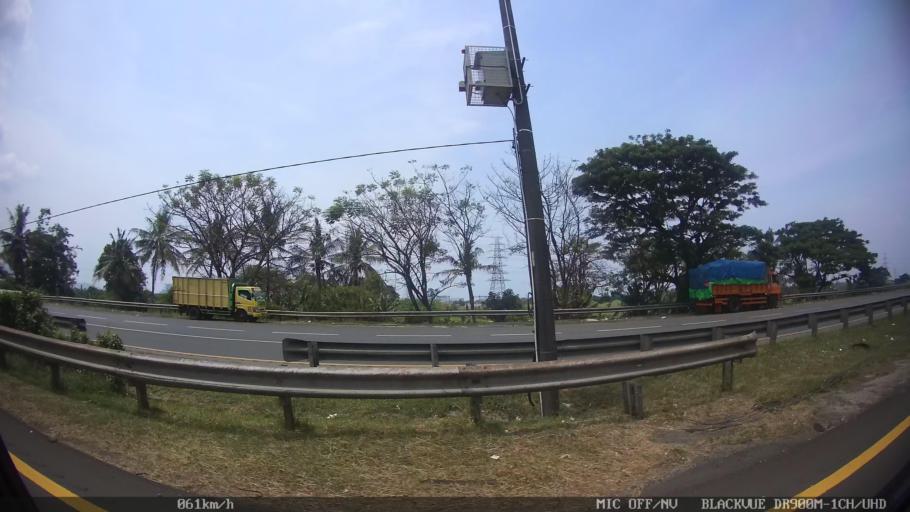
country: ID
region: Banten
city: Bojonegara
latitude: -6.0234
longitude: 106.0939
